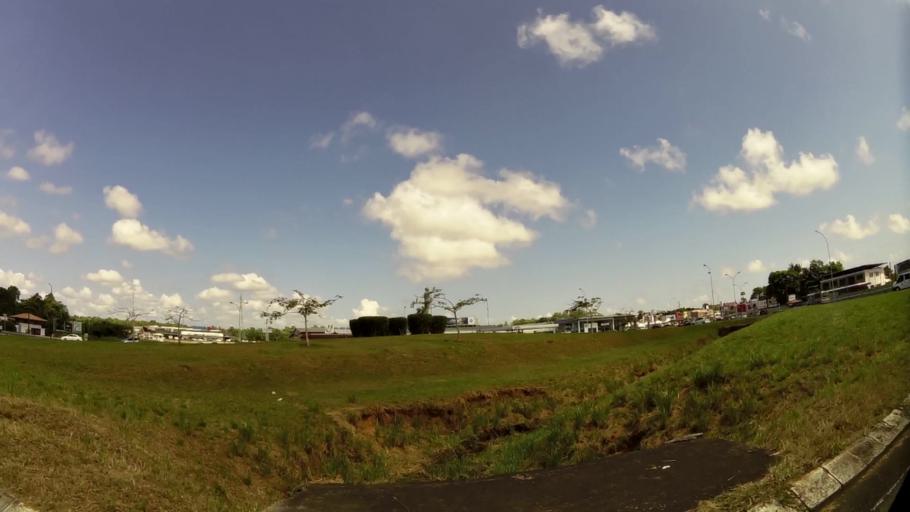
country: GF
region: Guyane
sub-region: Guyane
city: Cayenne
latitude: 4.9242
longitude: -52.3234
